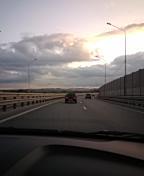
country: RU
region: Moskovskaya
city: Zhukovskiy
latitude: 55.5747
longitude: 38.1154
